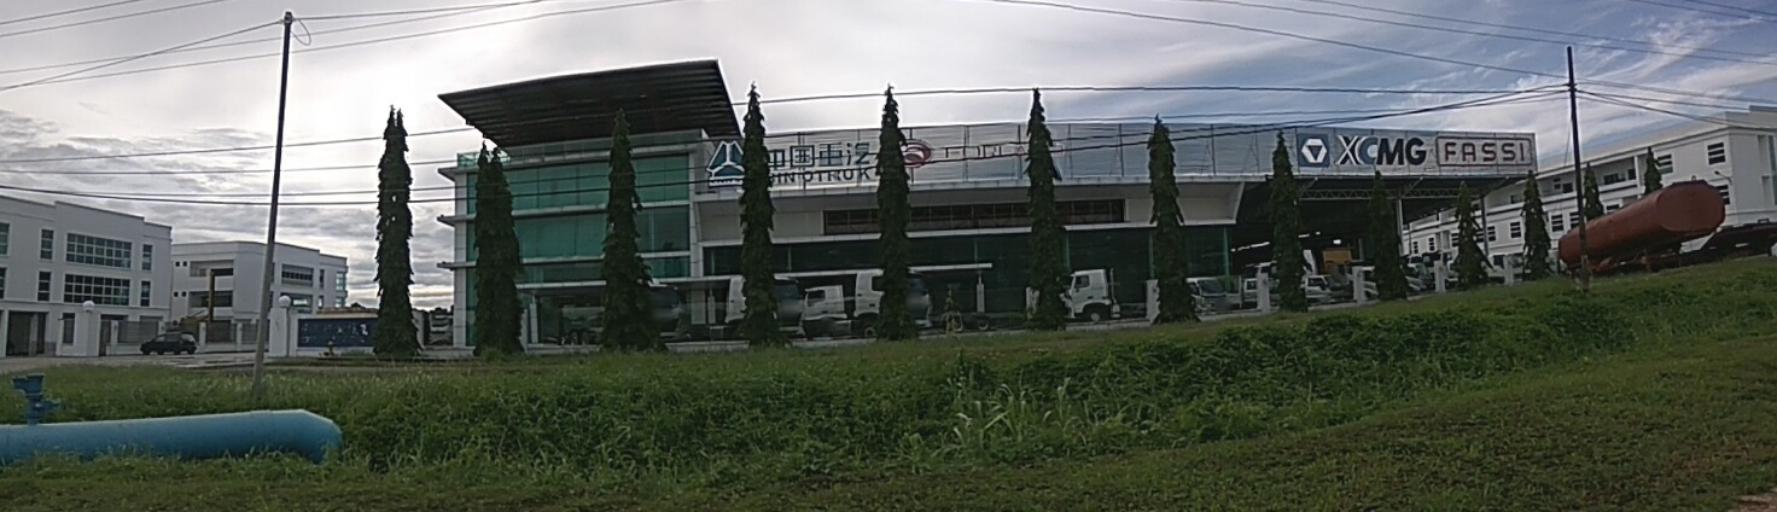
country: MY
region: Sarawak
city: Sibu
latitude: 2.2740
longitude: 111.8724
